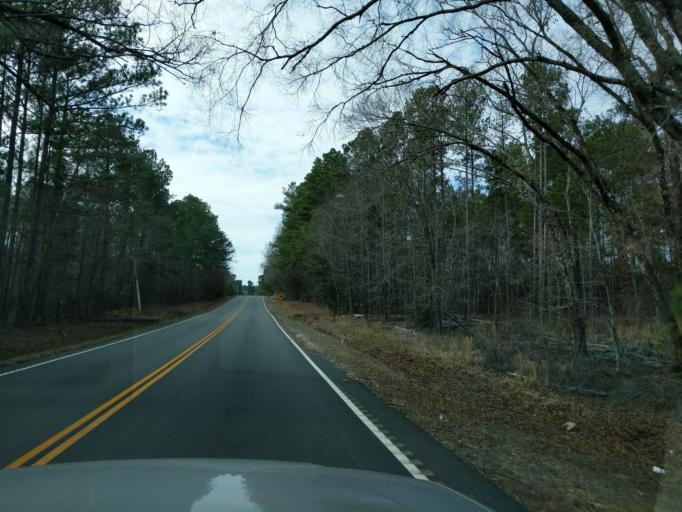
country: US
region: South Carolina
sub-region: Edgefield County
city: Edgefield
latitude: 33.9299
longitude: -81.9950
